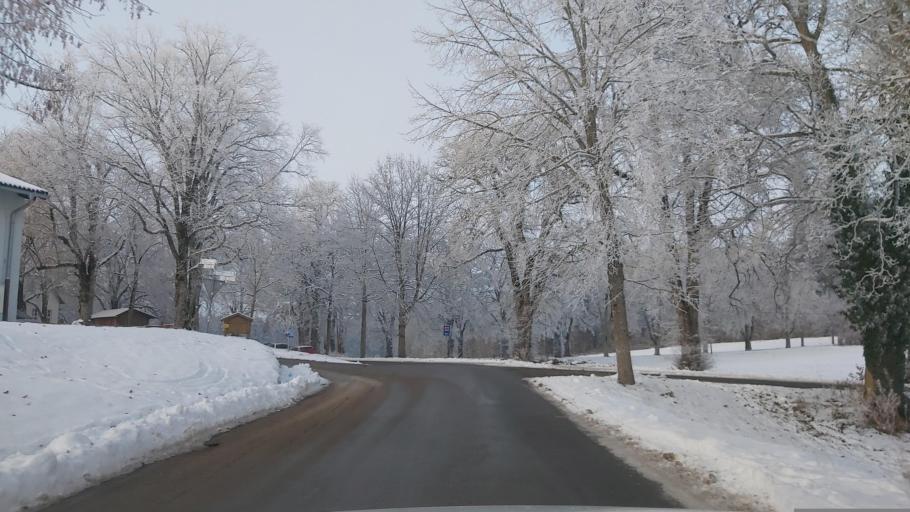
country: DE
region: Baden-Wuerttemberg
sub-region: Tuebingen Region
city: Sankt Johann
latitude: 48.4872
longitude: 9.3249
